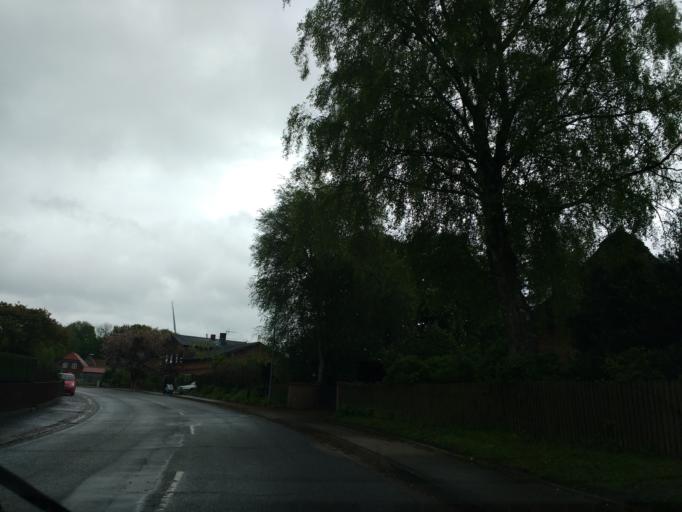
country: DE
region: Schleswig-Holstein
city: Loose
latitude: 54.5193
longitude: 9.8923
